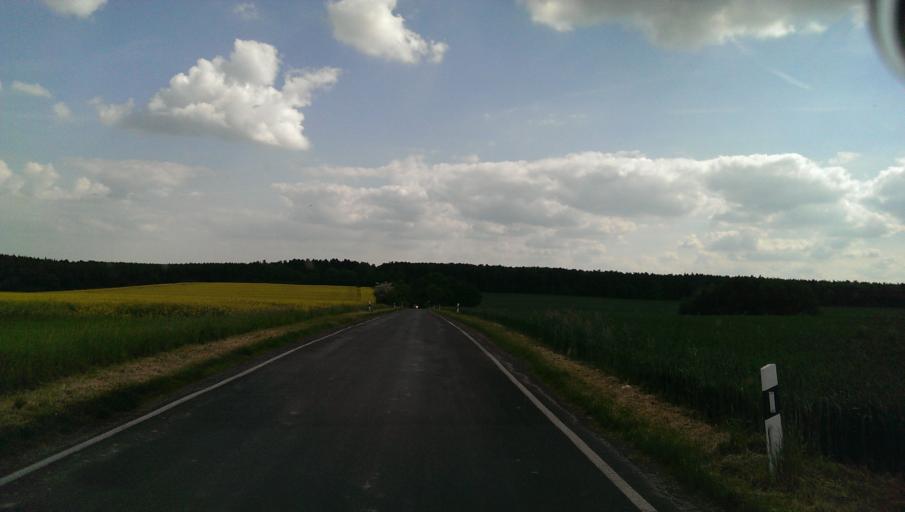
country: DE
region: Brandenburg
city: Wiesenburg
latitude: 52.1285
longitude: 12.5191
